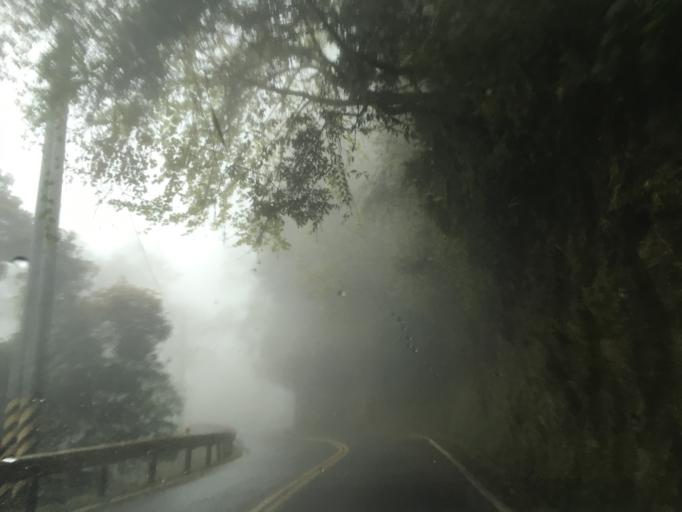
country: TW
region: Taiwan
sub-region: Hualien
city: Hualian
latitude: 24.1933
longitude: 121.4179
